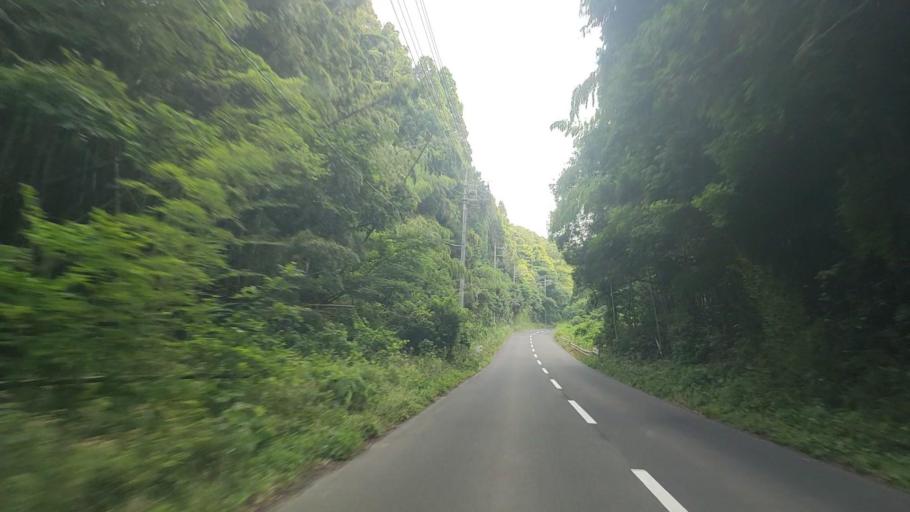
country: JP
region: Tottori
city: Kurayoshi
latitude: 35.4146
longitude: 133.7837
